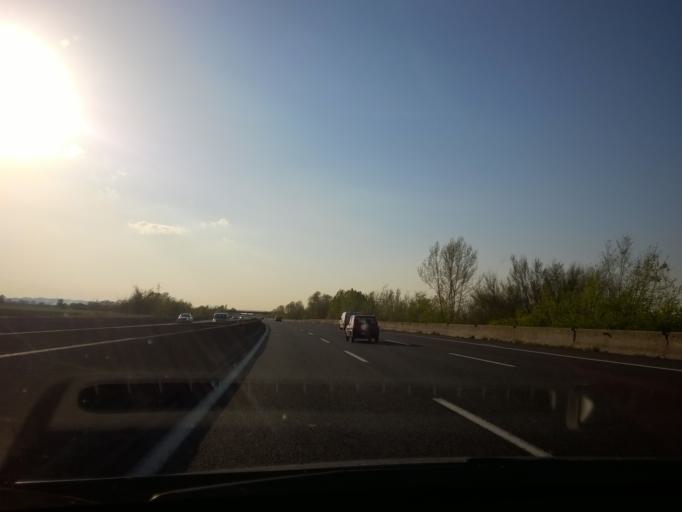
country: IT
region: Emilia-Romagna
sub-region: Provincia di Bologna
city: Osteria Grande
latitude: 44.4546
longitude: 11.5314
